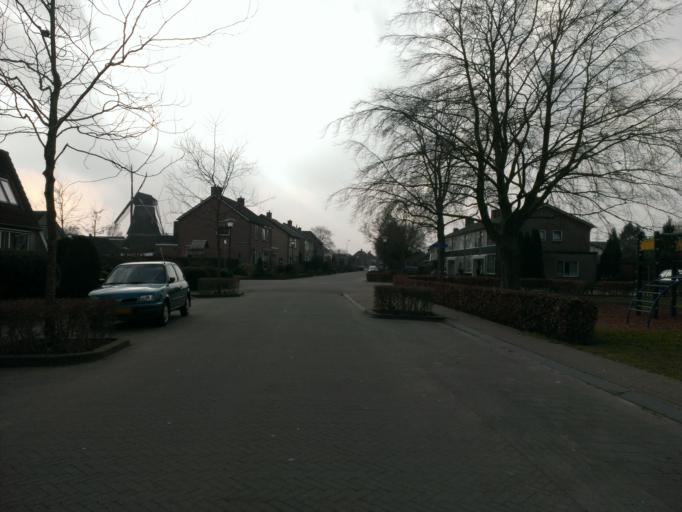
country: NL
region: Gelderland
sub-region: Gemeente Voorst
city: Twello
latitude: 52.2349
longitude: 6.0941
